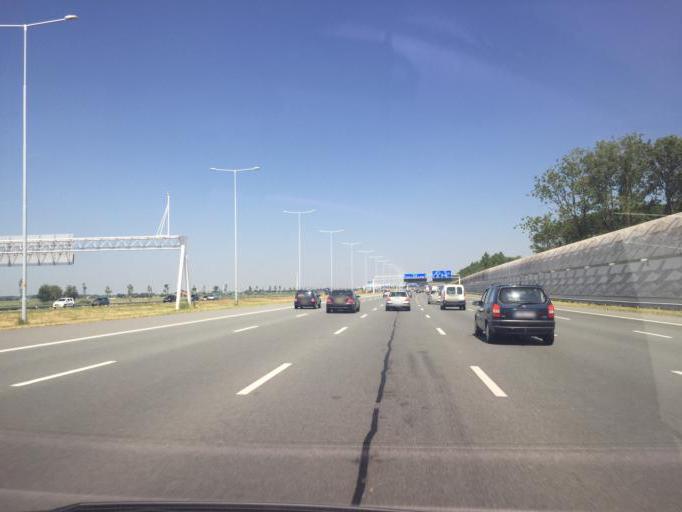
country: NL
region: North Holland
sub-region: Gemeente Amsterdam
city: Amsterdam-Zuidoost
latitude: 52.2668
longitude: 4.9617
